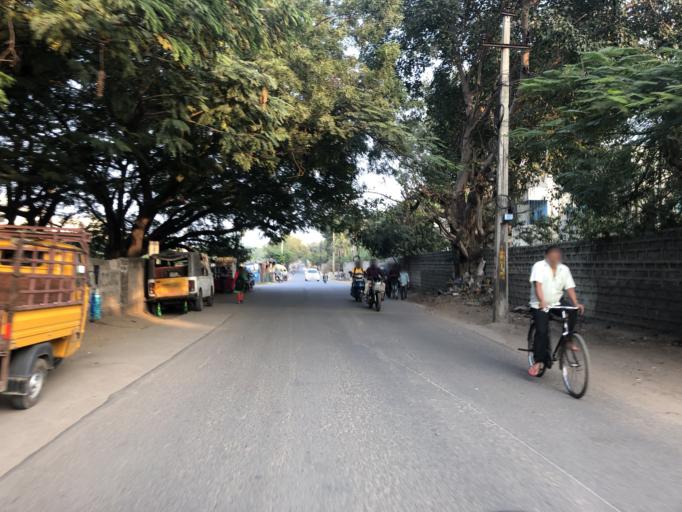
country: IN
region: Telangana
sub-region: Rangareddi
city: Kukatpalli
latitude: 17.4628
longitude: 78.4341
